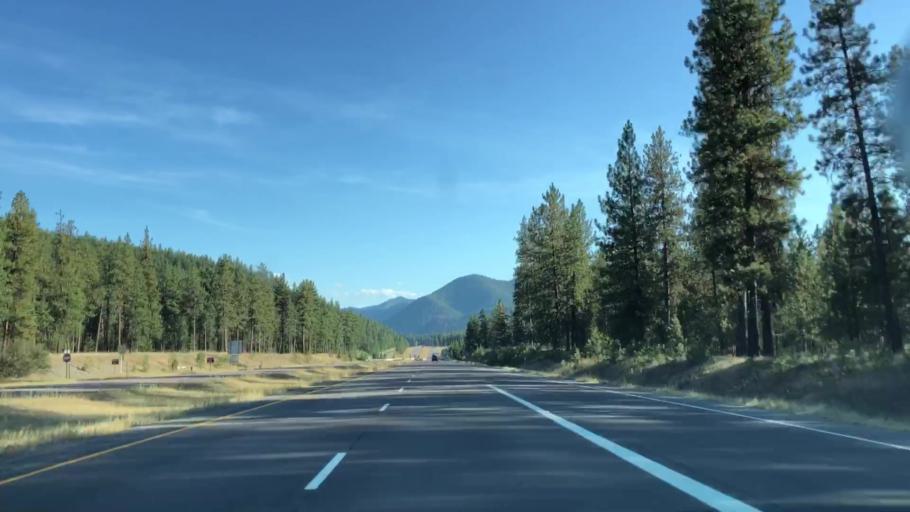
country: US
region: Montana
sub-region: Mineral County
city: Superior
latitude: 47.0734
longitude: -114.7658
